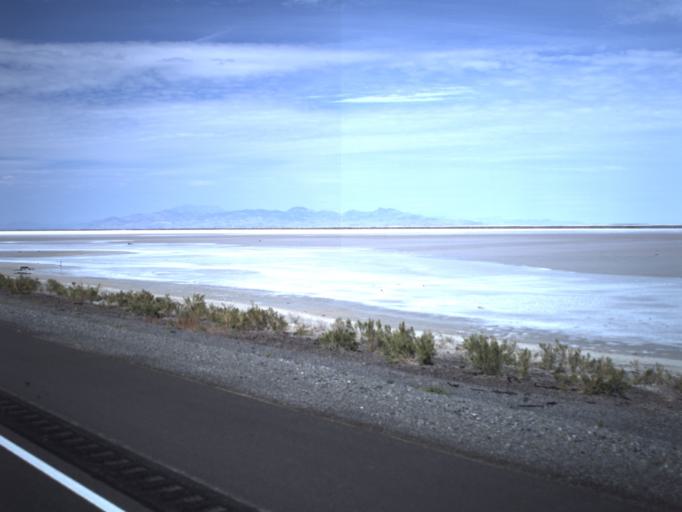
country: US
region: Utah
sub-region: Tooele County
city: Wendover
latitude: 40.7292
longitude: -113.3878
